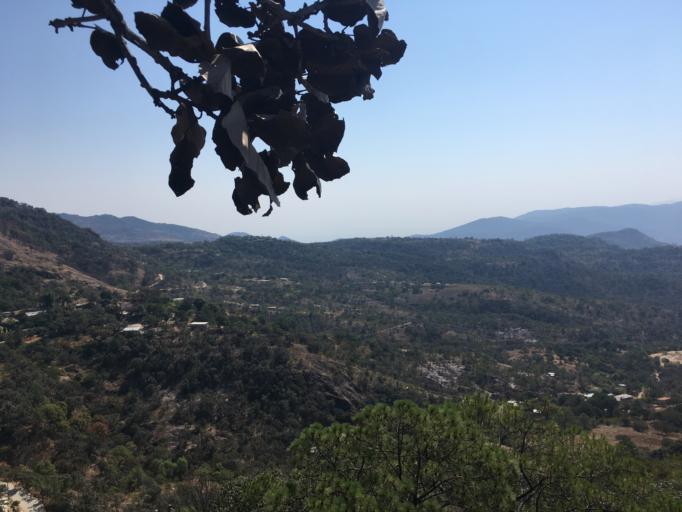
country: MX
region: Guerrero
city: Taxco de Alarcon
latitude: 18.5808
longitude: -99.6023
